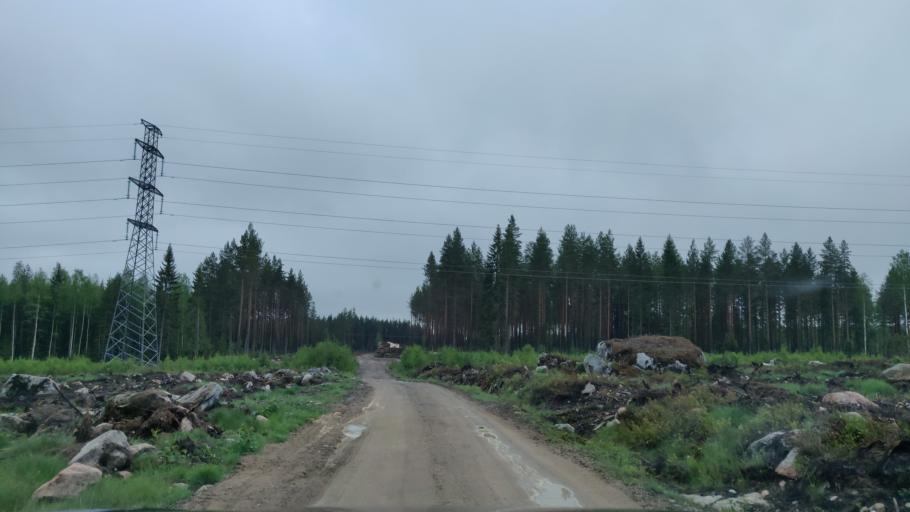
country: SE
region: Dalarna
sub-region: Avesta Kommun
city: Horndal
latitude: 60.3099
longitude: 16.4014
